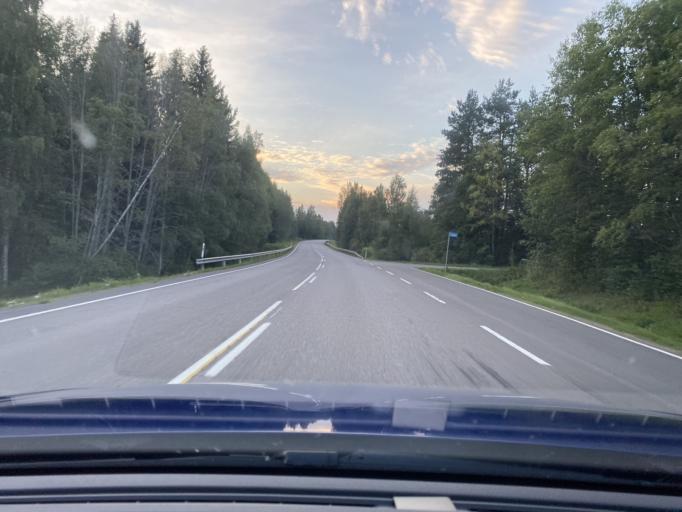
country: FI
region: Satakunta
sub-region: Pohjois-Satakunta
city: Honkajoki
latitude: 61.8825
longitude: 22.2930
